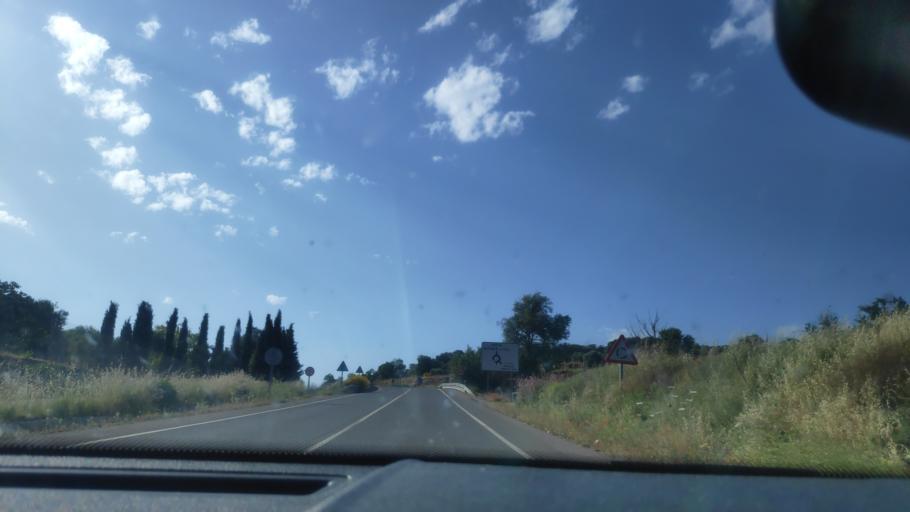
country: ES
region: Andalusia
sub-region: Provincia de Jaen
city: Alcala la Real
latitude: 37.4516
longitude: -3.8917
